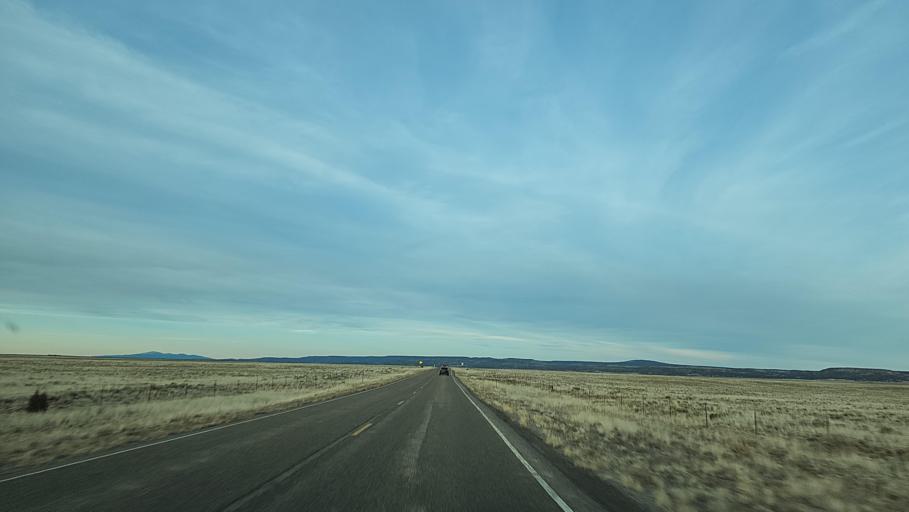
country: US
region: New Mexico
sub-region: Cibola County
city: Grants
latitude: 34.6756
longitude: -108.0857
